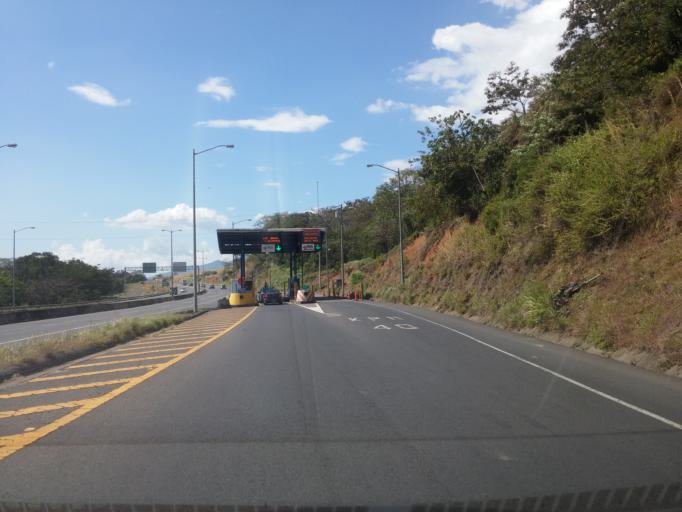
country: CR
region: Heredia
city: Colon
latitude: 9.9649
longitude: -84.2824
